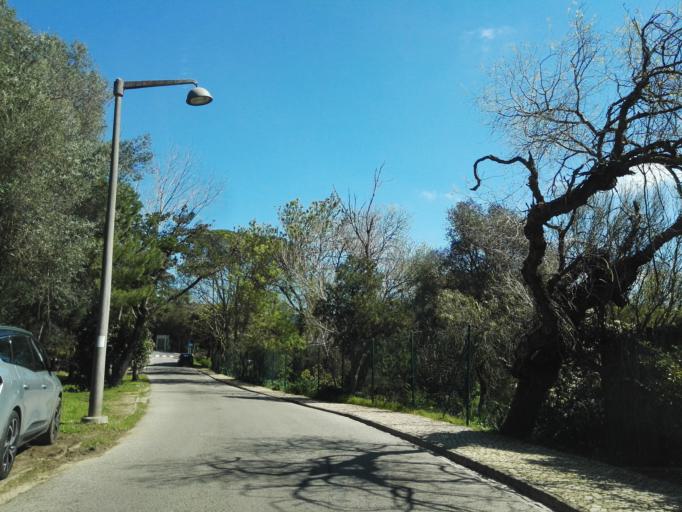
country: PT
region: Lisbon
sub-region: Sintra
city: Rio de Mouro
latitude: 38.7511
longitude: -9.3491
